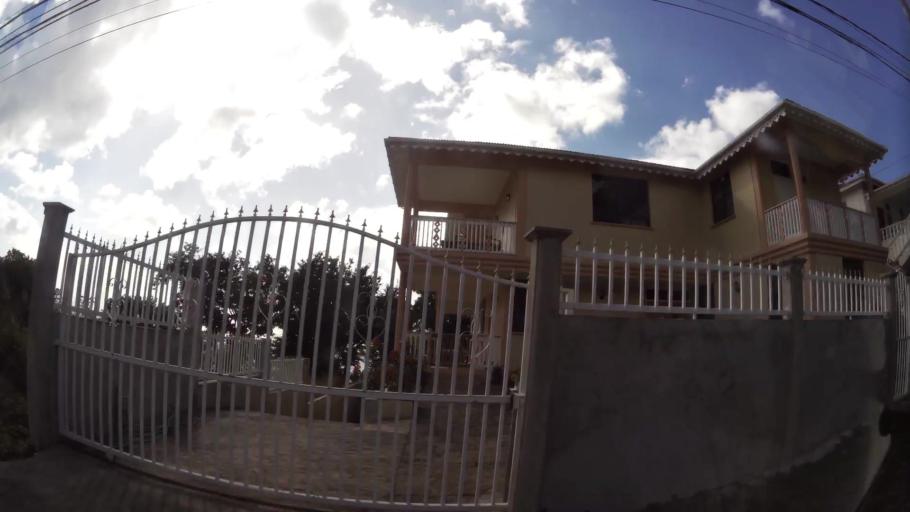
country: DM
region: Saint George
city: Roseau
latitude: 15.2871
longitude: -61.3750
